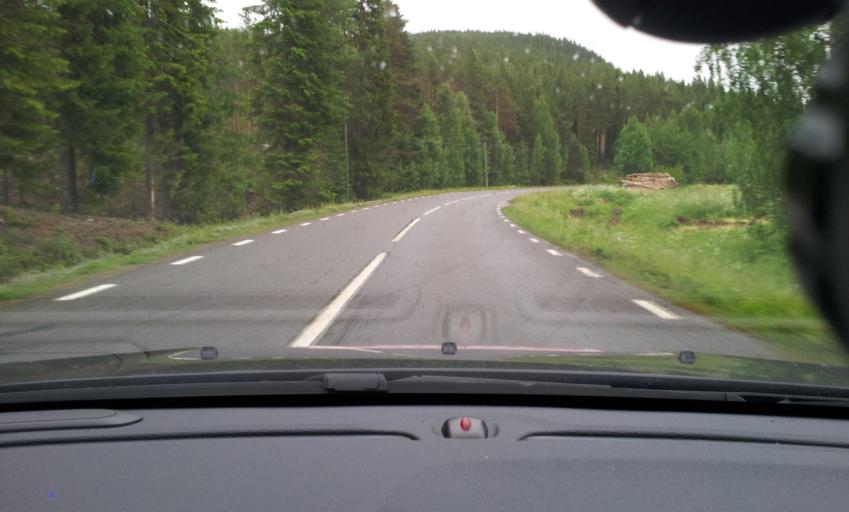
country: SE
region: Jaemtland
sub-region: Stroemsunds Kommun
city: Stroemsund
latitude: 63.4116
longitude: 15.6119
